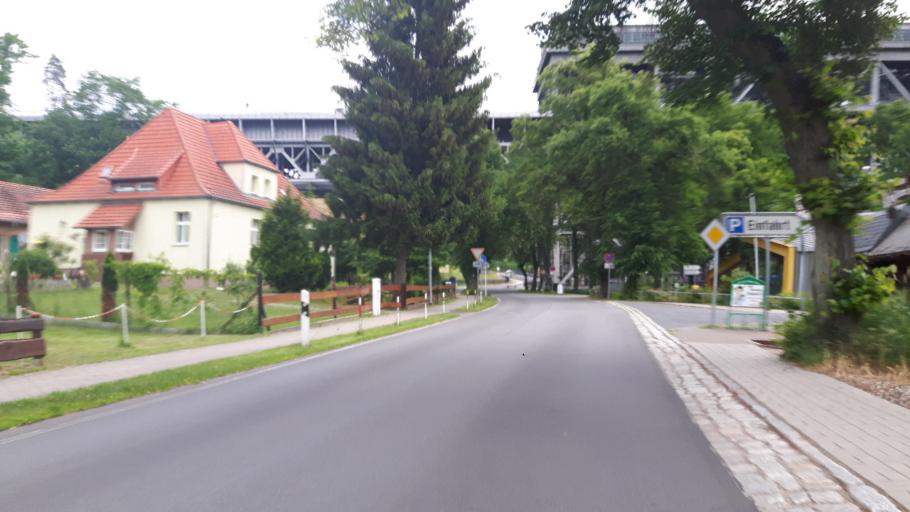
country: DE
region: Brandenburg
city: Niederfinow
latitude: 52.8479
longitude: 13.9401
